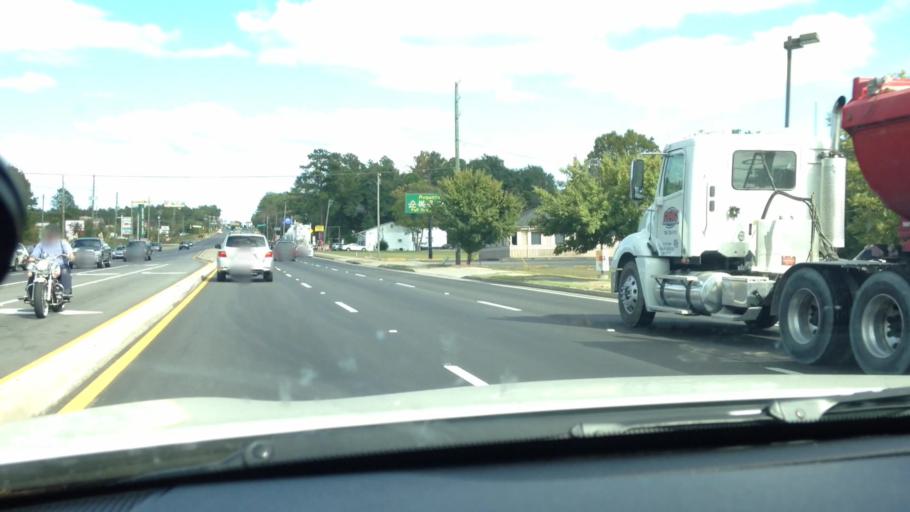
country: US
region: Georgia
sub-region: Columbia County
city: Martinez
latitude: 33.4189
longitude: -82.0786
